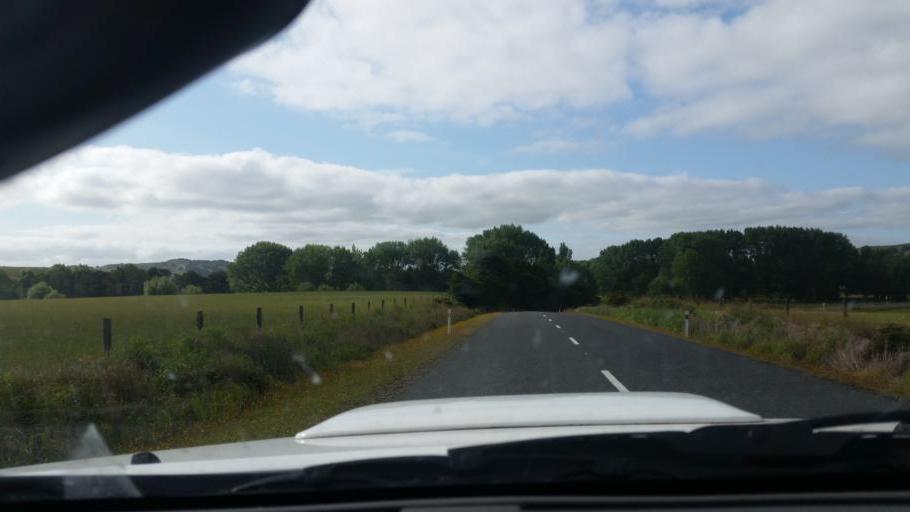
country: NZ
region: Northland
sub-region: Kaipara District
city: Dargaville
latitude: -35.8380
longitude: 173.8441
